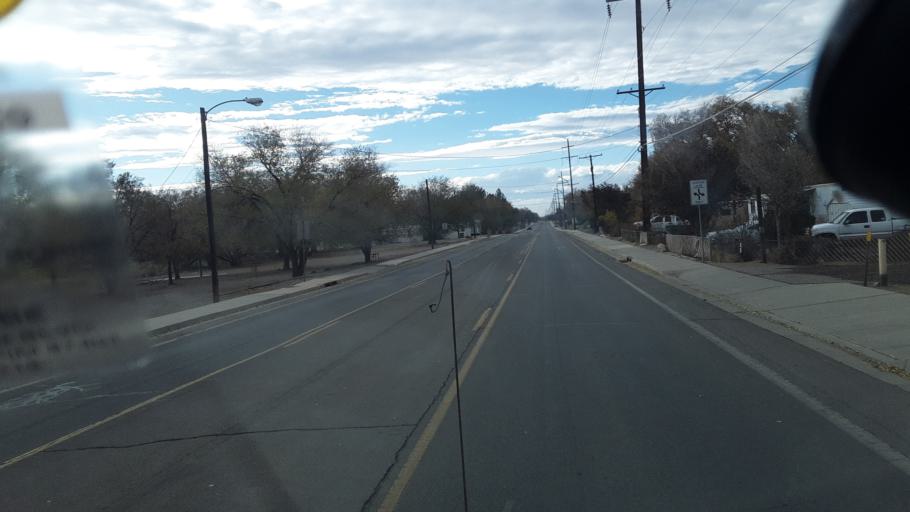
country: US
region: New Mexico
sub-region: San Juan County
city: Farmington
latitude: 36.7265
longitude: -108.1739
